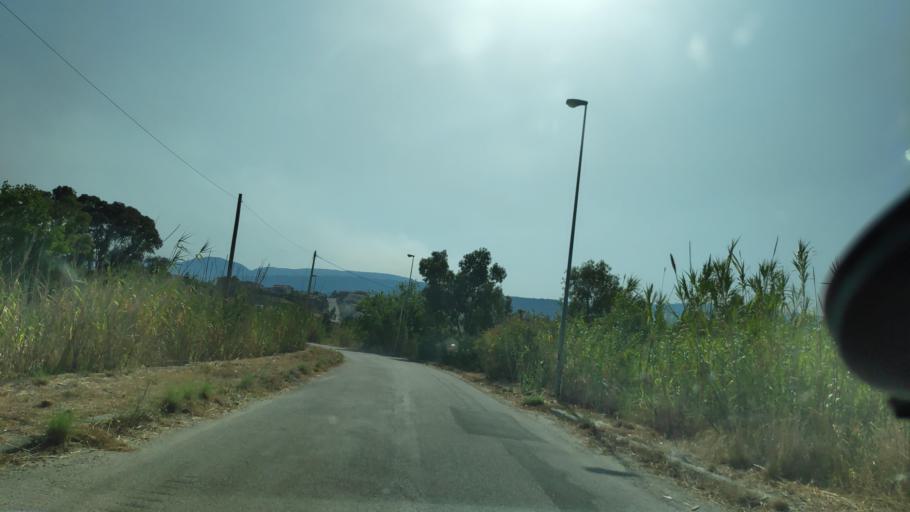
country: IT
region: Calabria
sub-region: Provincia di Catanzaro
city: Badolato Marina
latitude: 38.5893
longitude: 16.5672
